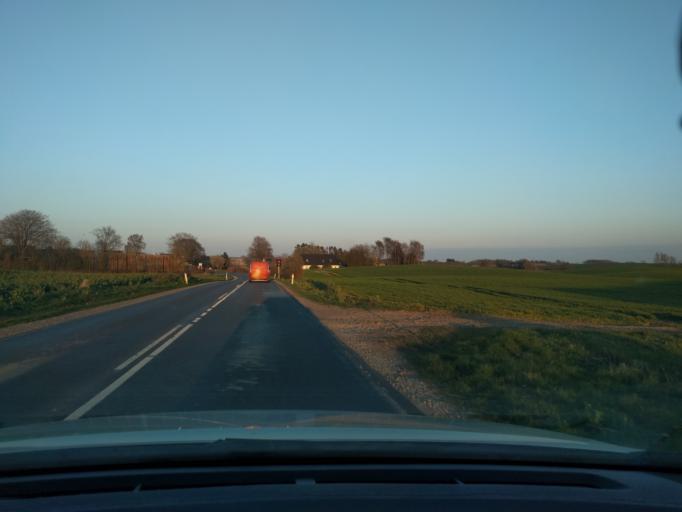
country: DK
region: South Denmark
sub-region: Assens Kommune
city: Glamsbjerg
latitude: 55.2715
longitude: 10.0594
